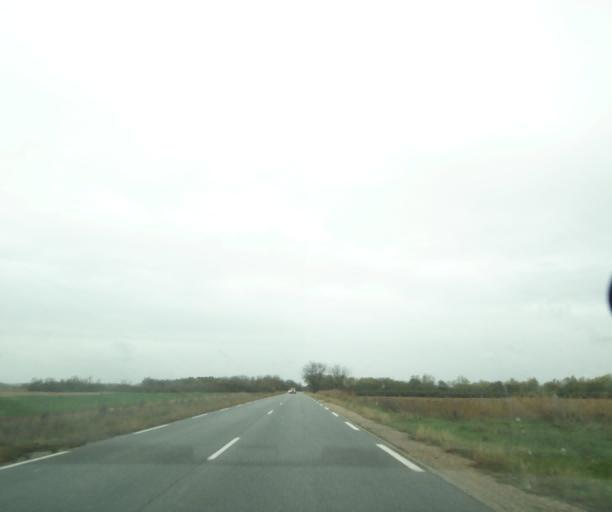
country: FR
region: Rhone-Alpes
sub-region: Departement de l'Ain
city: Loyettes
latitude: 45.7864
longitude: 5.2322
